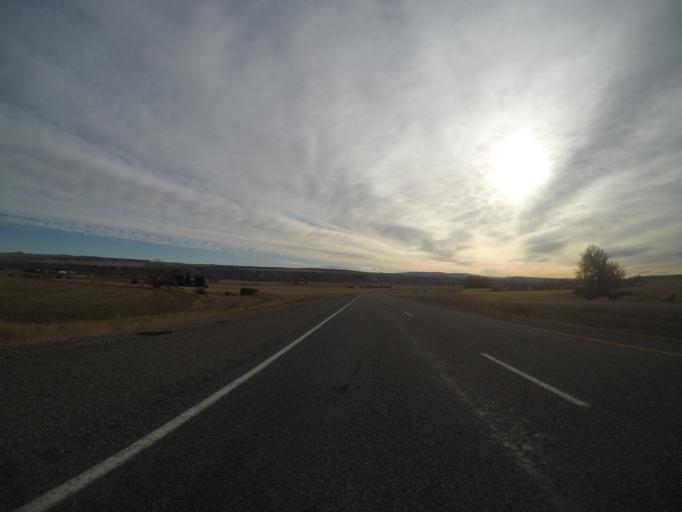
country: US
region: Montana
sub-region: Yellowstone County
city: Laurel
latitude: 45.5417
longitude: -108.8557
